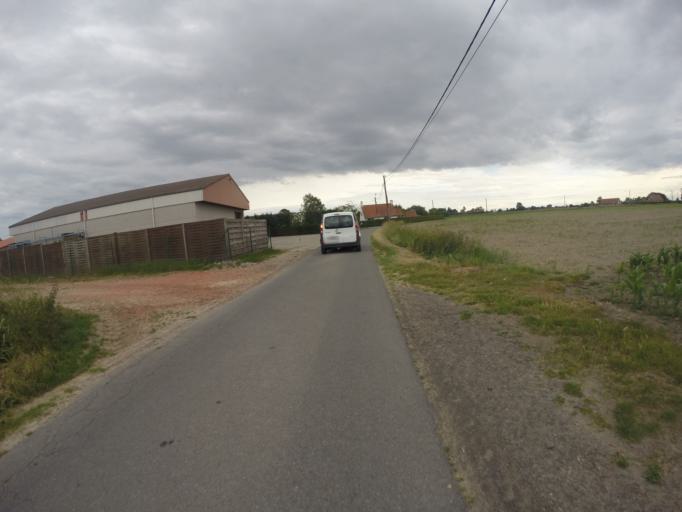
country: BE
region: Flanders
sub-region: Provincie West-Vlaanderen
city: Ruiselede
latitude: 51.0516
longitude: 3.3580
